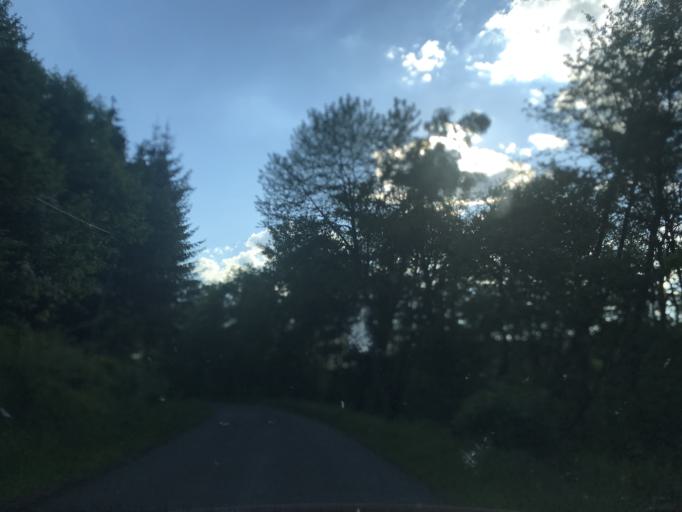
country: FR
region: Auvergne
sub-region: Departement du Puy-de-Dome
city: Job
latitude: 45.7057
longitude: 3.6970
